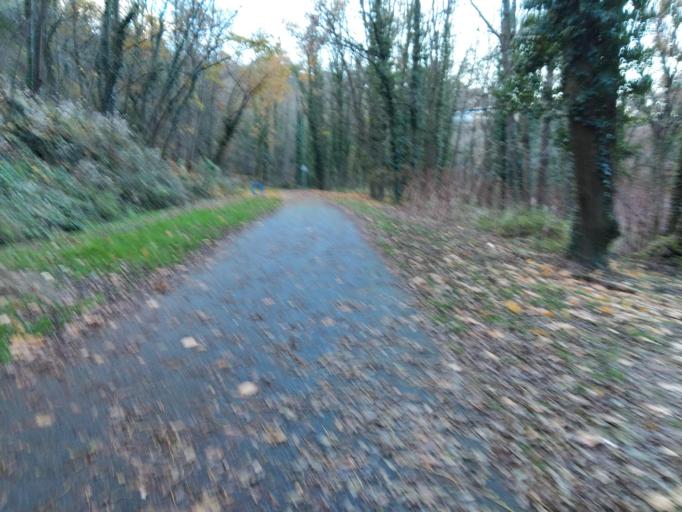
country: FR
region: Rhone-Alpes
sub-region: Departement de l'Ardeche
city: Annonay
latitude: 45.2501
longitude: 4.6788
